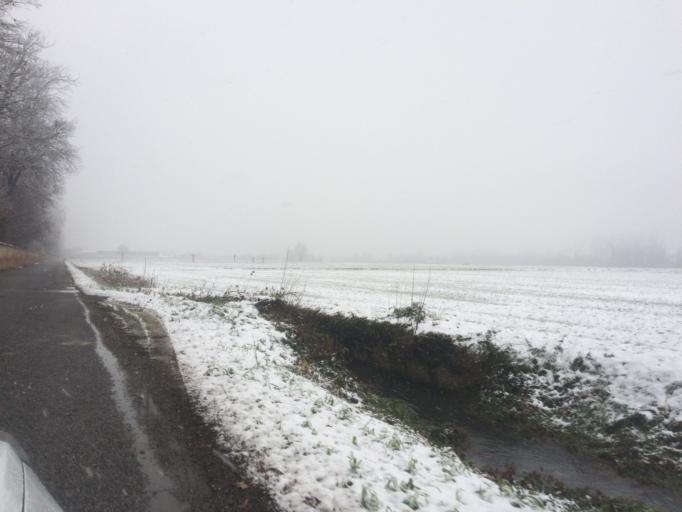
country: IT
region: Piedmont
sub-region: Provincia di Cuneo
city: Racconigi
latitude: 44.7760
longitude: 7.6698
